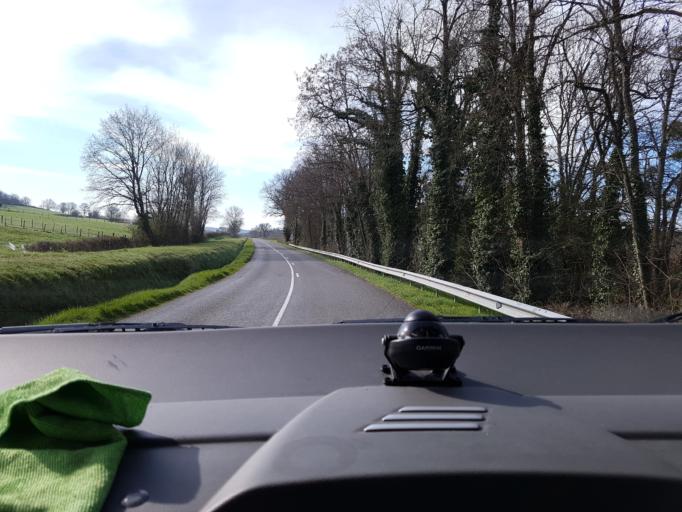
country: FR
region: Bourgogne
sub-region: Departement de Saone-et-Loire
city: Toulon-sur-Arroux
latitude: 46.7264
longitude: 4.1298
